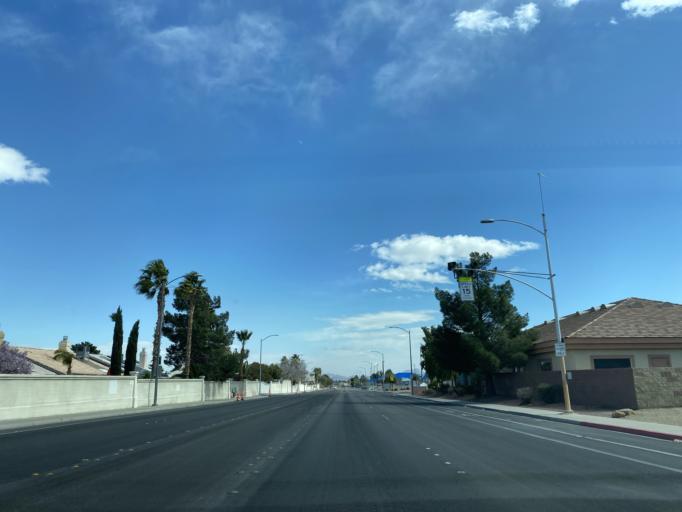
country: US
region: Nevada
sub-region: Clark County
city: Spring Valley
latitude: 36.2259
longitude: -115.2688
